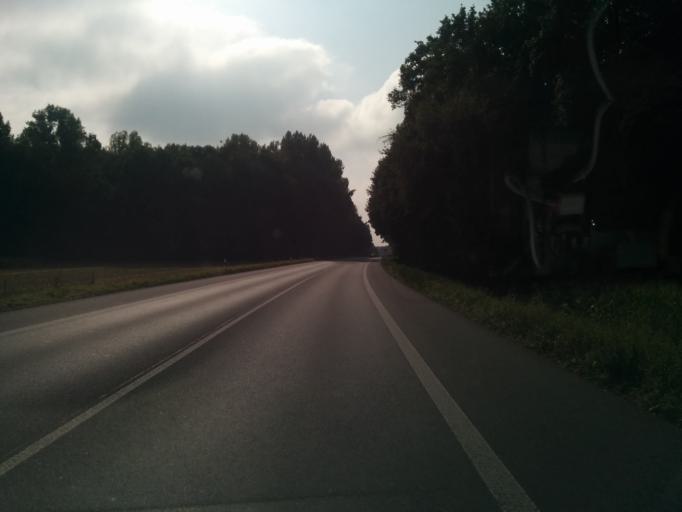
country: DE
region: North Rhine-Westphalia
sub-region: Regierungsbezirk Munster
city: Dulmen
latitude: 51.8782
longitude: 7.2189
